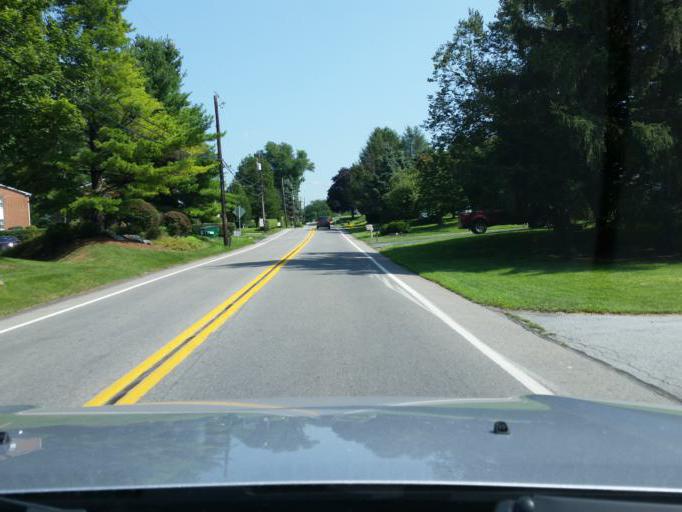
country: US
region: Pennsylvania
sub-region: Dauphin County
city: Hershey
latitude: 40.2631
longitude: -76.6418
